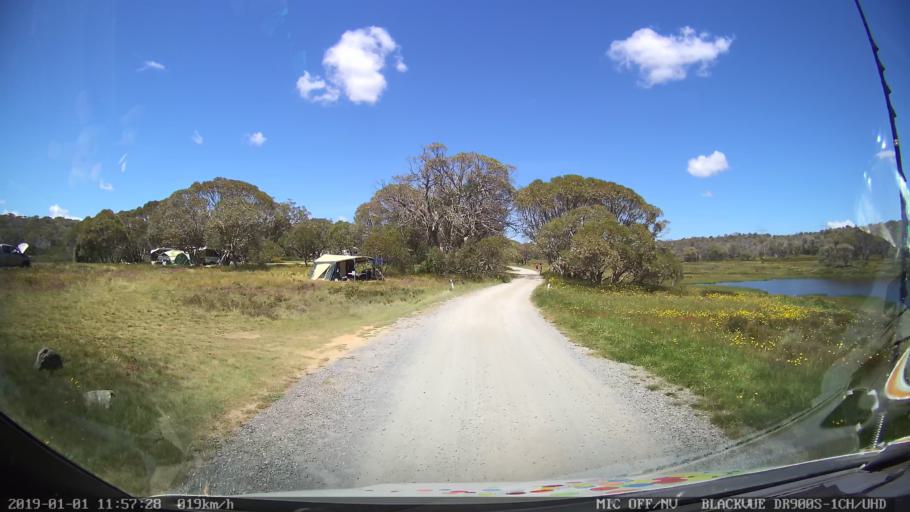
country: AU
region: New South Wales
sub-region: Snowy River
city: Jindabyne
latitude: -35.8877
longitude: 148.4490
